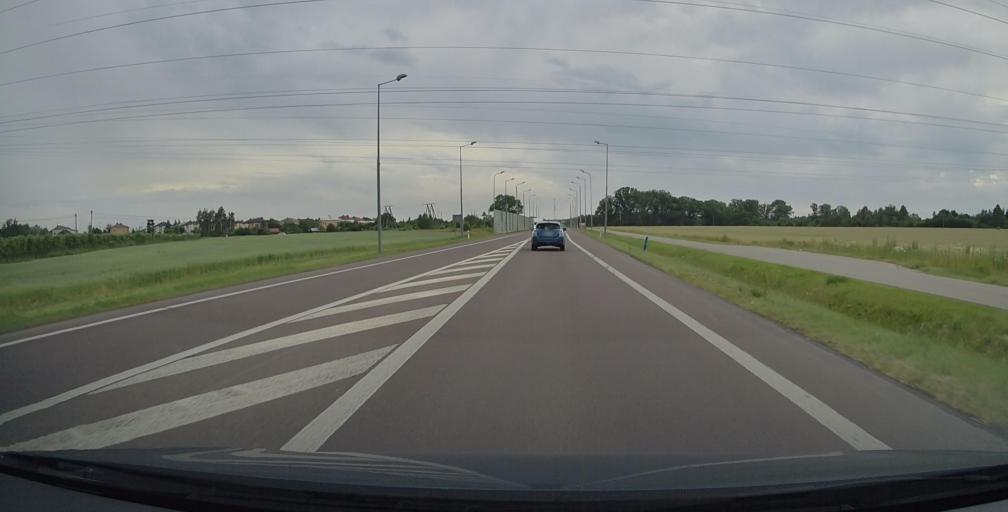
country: PL
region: Lublin Voivodeship
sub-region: Biala Podlaska
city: Biala Podlaska
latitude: 52.0444
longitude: 23.0939
